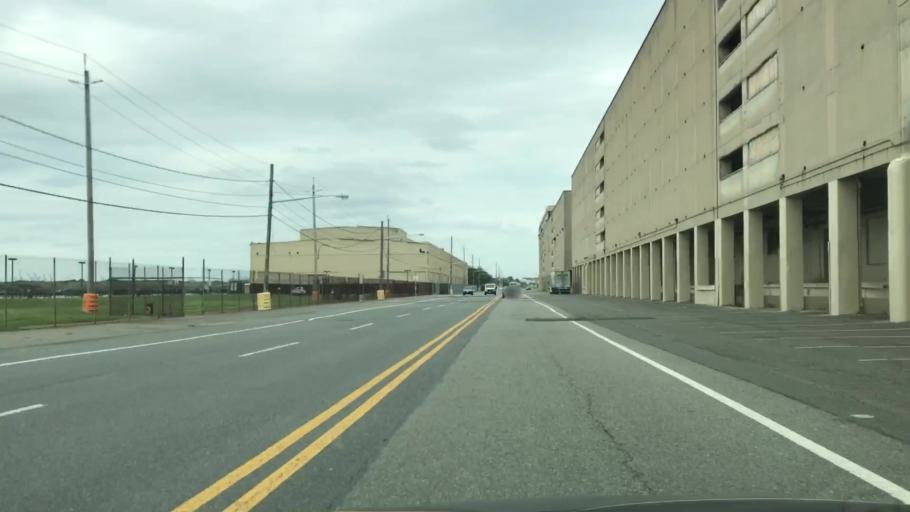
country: US
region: New Jersey
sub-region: Hudson County
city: Bayonne
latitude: 40.6654
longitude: -74.0805
